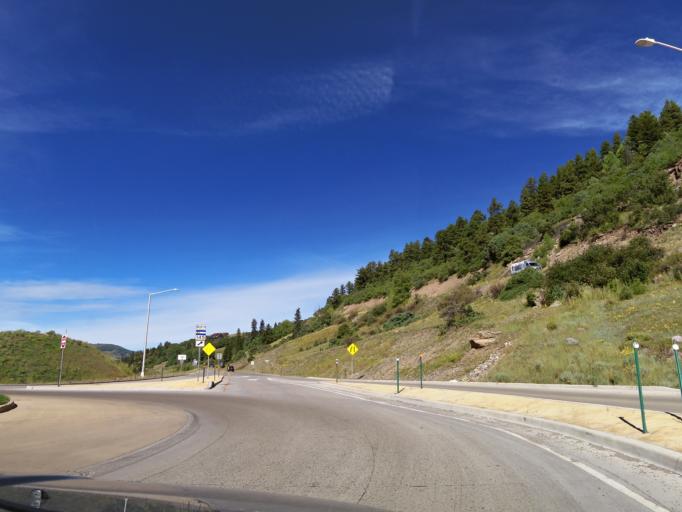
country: US
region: Colorado
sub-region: San Miguel County
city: Mountain Village
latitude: 37.9505
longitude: -107.8713
